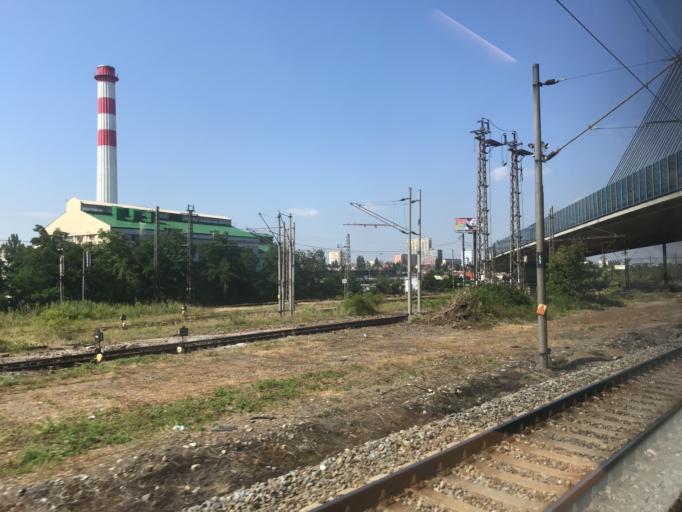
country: CZ
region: Praha
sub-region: Praha 9
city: Vysocany
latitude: 50.0618
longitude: 14.5117
